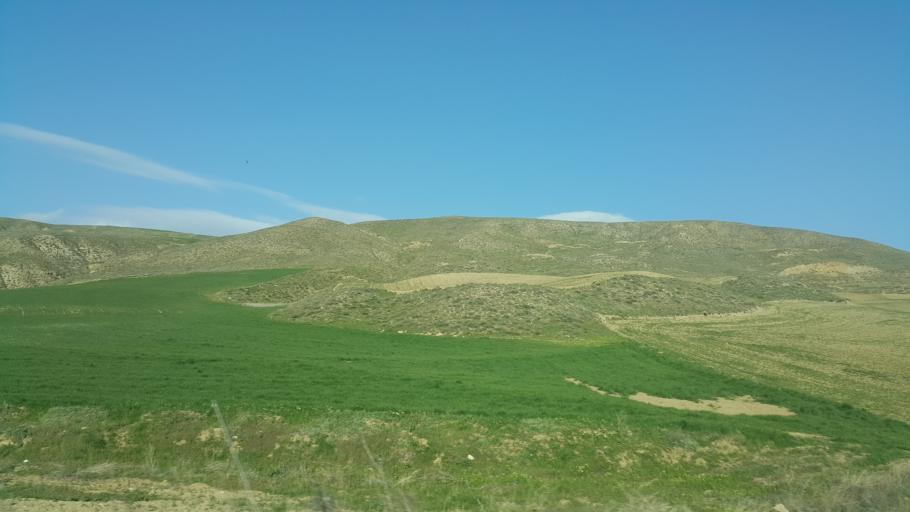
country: TR
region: Ankara
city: Sereflikochisar
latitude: 39.0265
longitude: 33.4481
